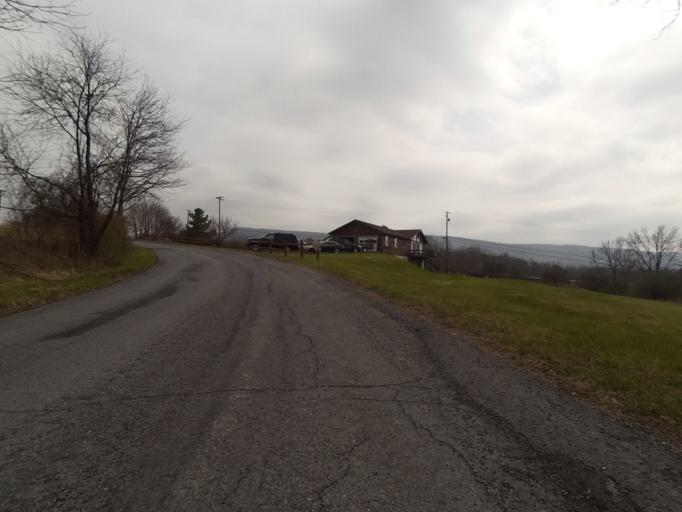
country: US
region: Pennsylvania
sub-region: Centre County
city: Boalsburg
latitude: 40.7908
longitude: -77.7972
